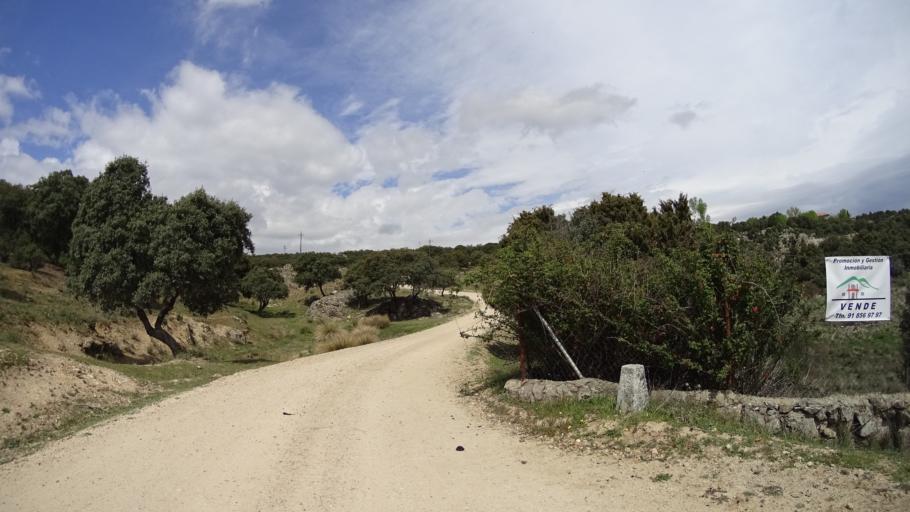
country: ES
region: Madrid
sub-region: Provincia de Madrid
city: Hoyo de Manzanares
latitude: 40.6198
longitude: -3.8829
